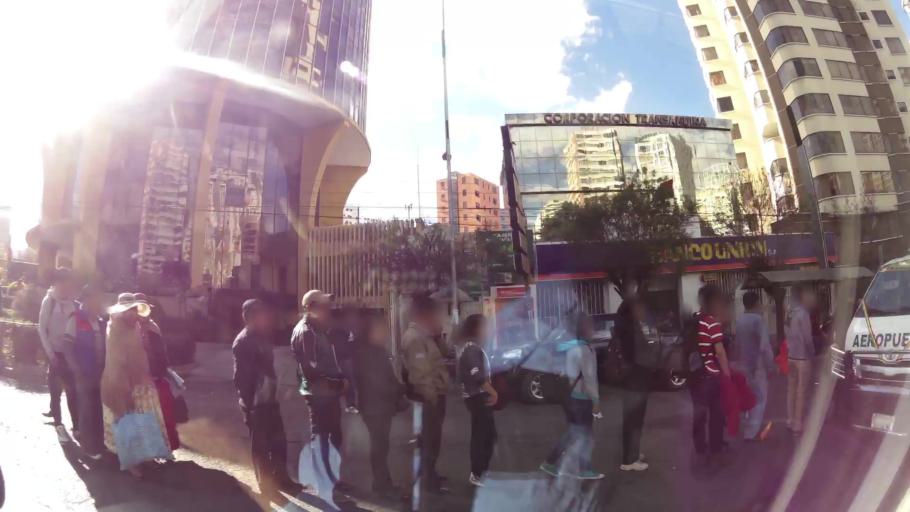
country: BO
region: La Paz
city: La Paz
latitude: -16.5090
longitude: -68.1244
